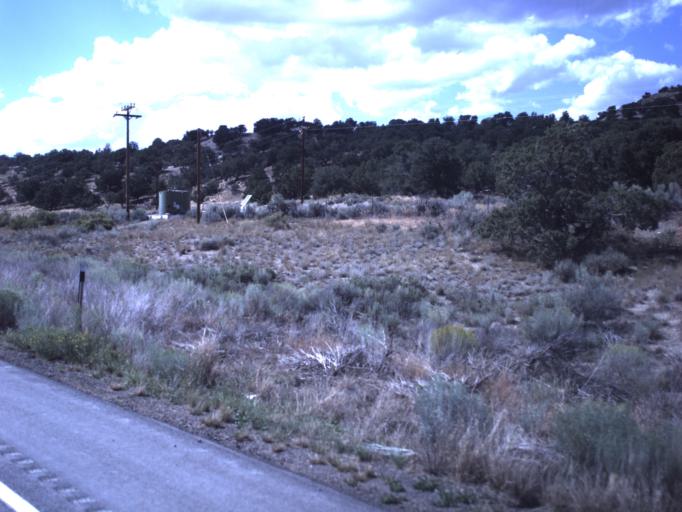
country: US
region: Utah
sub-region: Duchesne County
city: Duchesne
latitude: 40.1725
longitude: -110.5841
